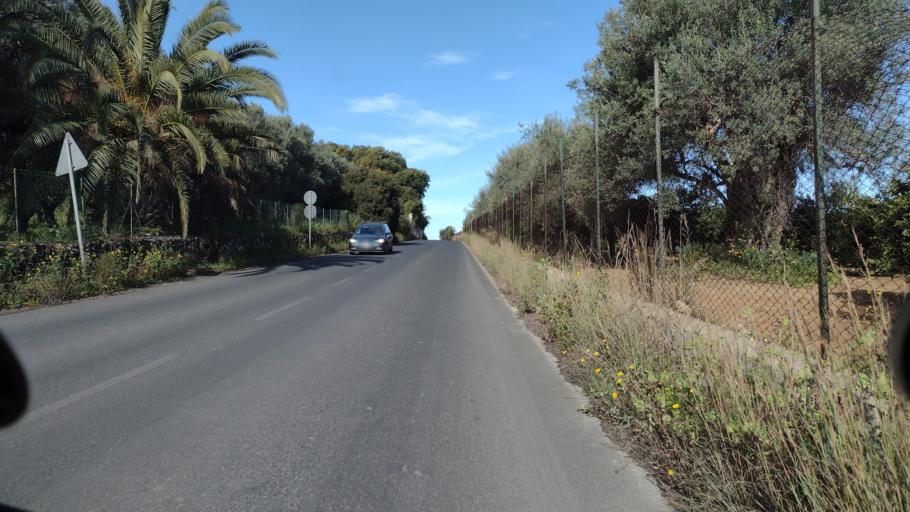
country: IT
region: Sicily
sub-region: Provincia di Siracusa
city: Noto
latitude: 36.8762
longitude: 15.1024
